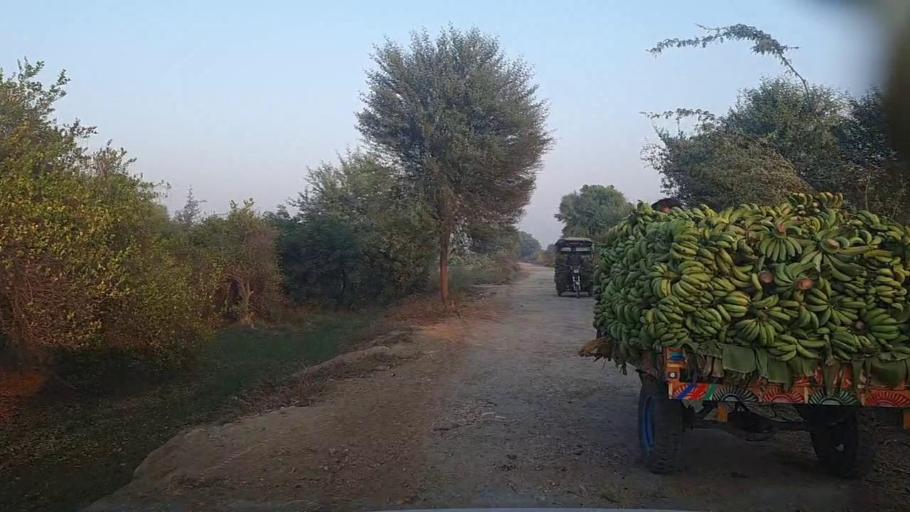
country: PK
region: Sindh
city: Karaundi
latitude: 26.8430
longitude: 68.3578
